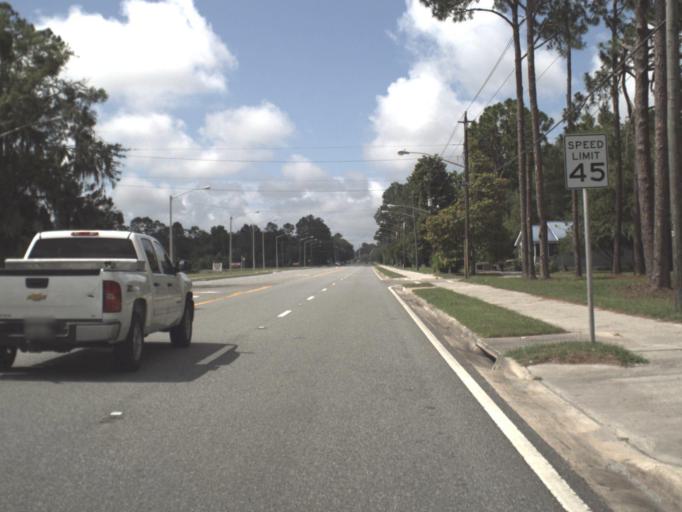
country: US
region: Florida
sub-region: Columbia County
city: Five Points
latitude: 30.2329
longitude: -82.6387
